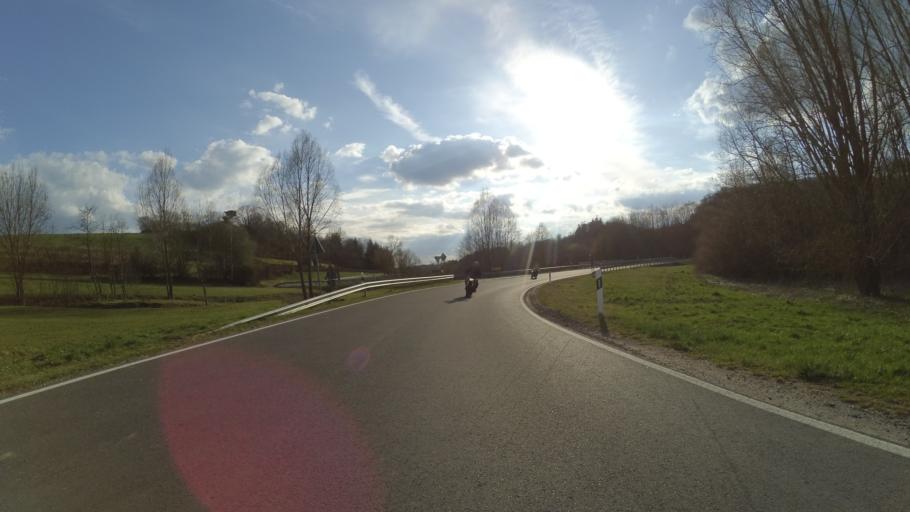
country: DE
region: Rheinland-Pfalz
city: Steiningen
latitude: 50.1879
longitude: 6.9103
